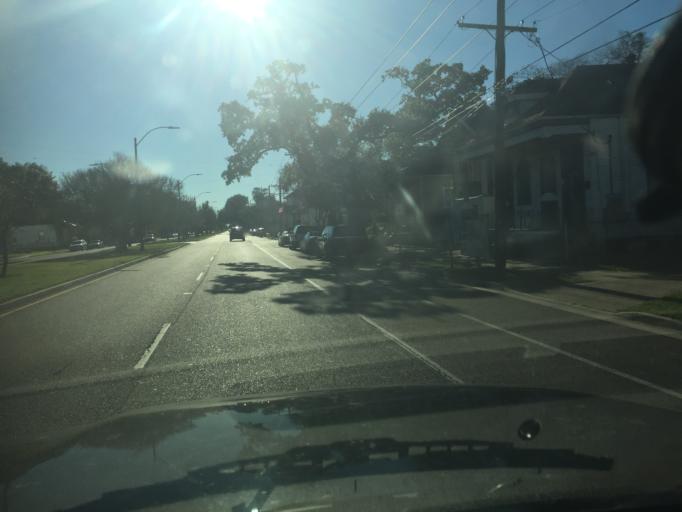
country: US
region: Louisiana
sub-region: Orleans Parish
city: New Orleans
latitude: 29.9822
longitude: -90.0729
